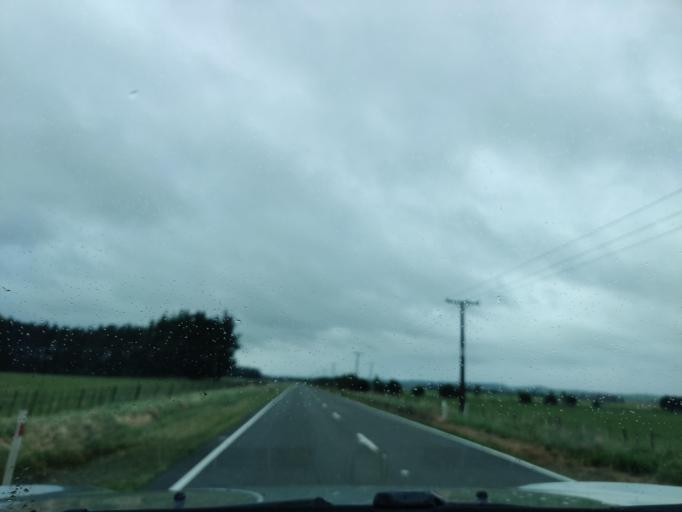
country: NZ
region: Hawke's Bay
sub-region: Hastings District
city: Hastings
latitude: -40.0086
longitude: 176.3813
